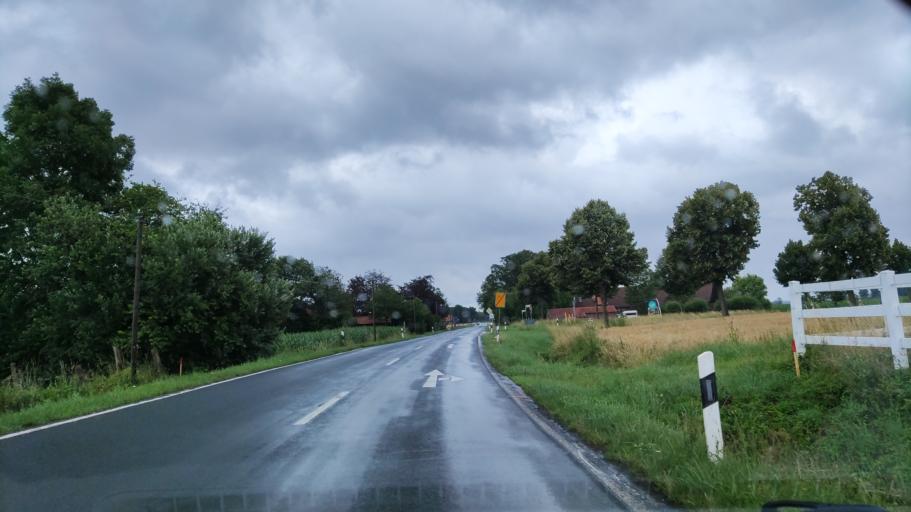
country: DE
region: North Rhine-Westphalia
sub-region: Regierungsbezirk Munster
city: Telgte
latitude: 51.8960
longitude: 7.7555
